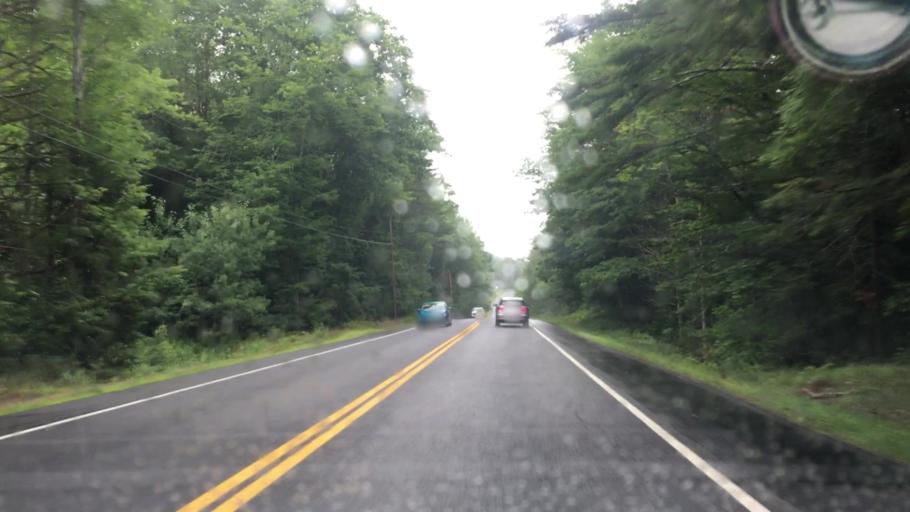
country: US
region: Maine
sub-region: Knox County
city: Union
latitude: 44.2259
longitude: -69.3318
